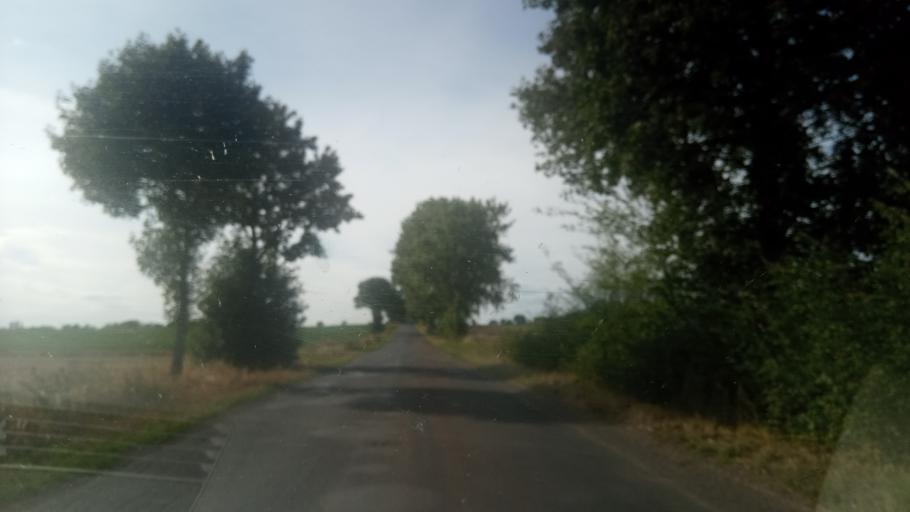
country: PL
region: Kujawsko-Pomorskie
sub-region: Powiat nakielski
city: Sadki
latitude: 53.2049
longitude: 17.3719
